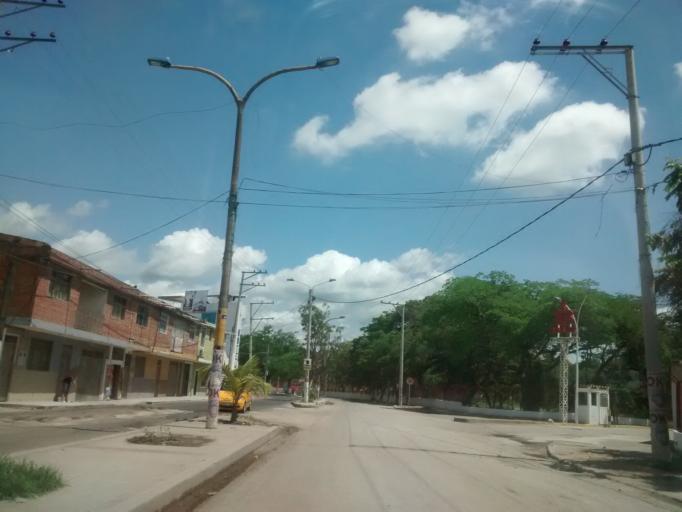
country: CO
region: Cundinamarca
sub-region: Girardot
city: Girardot City
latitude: 4.3005
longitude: -74.7985
